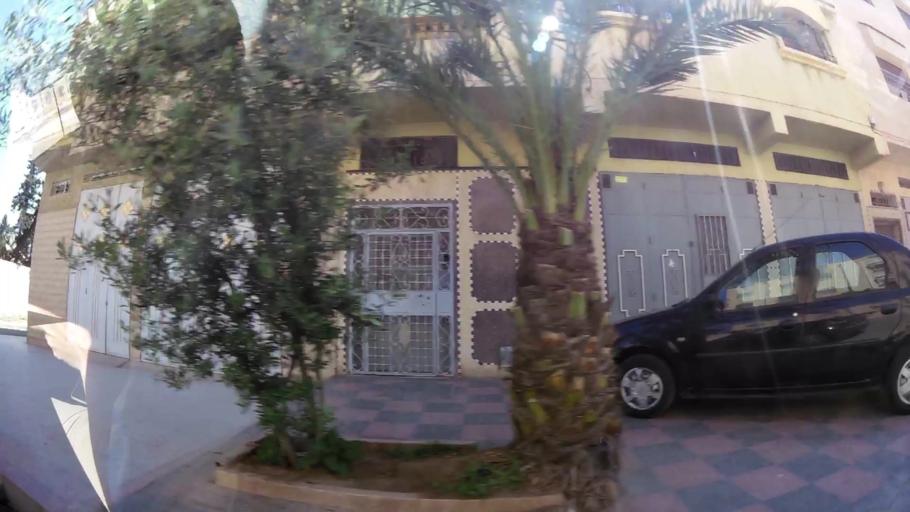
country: MA
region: Oriental
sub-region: Oujda-Angad
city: Oujda
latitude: 34.6870
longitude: -1.9391
